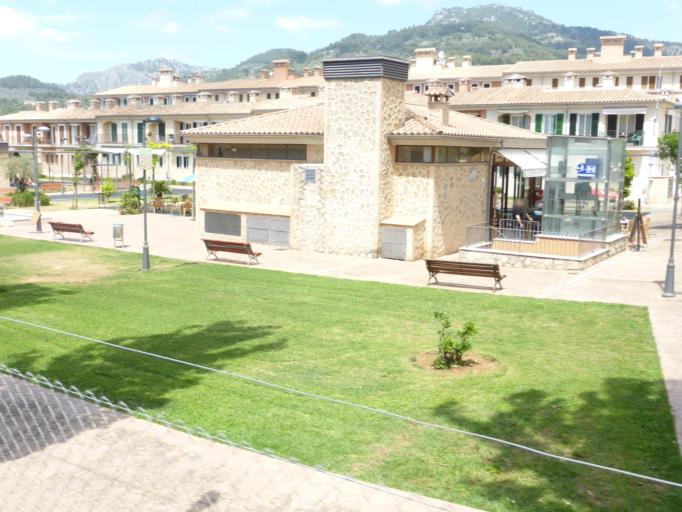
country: ES
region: Balearic Islands
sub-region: Illes Balears
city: Soller
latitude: 39.7698
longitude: 2.7123
